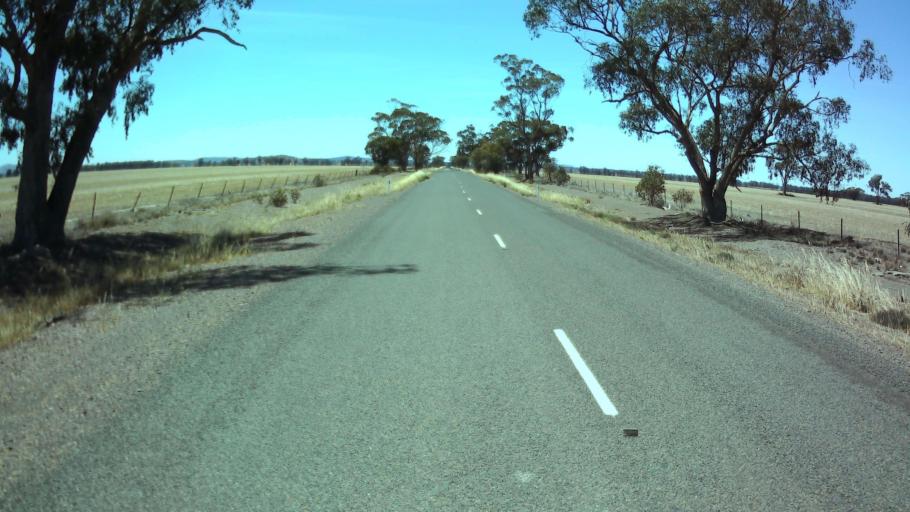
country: AU
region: New South Wales
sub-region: Bland
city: West Wyalong
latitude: -33.6582
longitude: 147.5797
